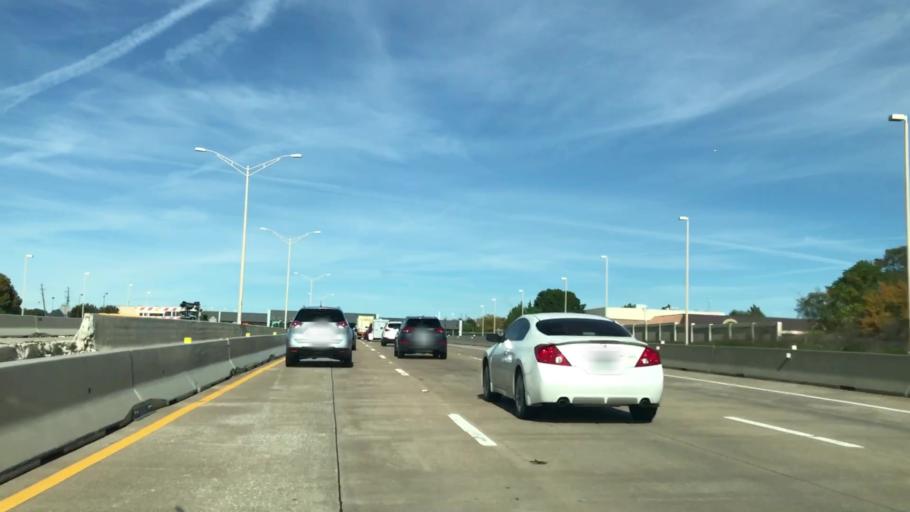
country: US
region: Texas
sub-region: Dallas County
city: Addison
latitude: 32.9903
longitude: -96.8638
